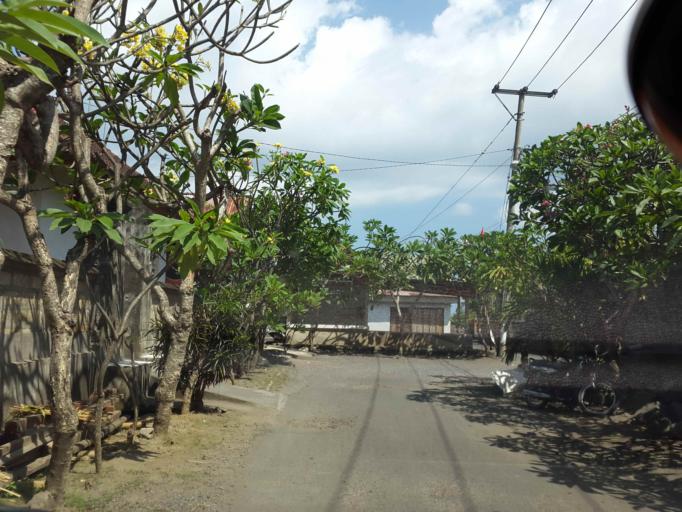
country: ID
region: Bali
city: Klungkung
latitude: -8.5657
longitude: 115.3783
